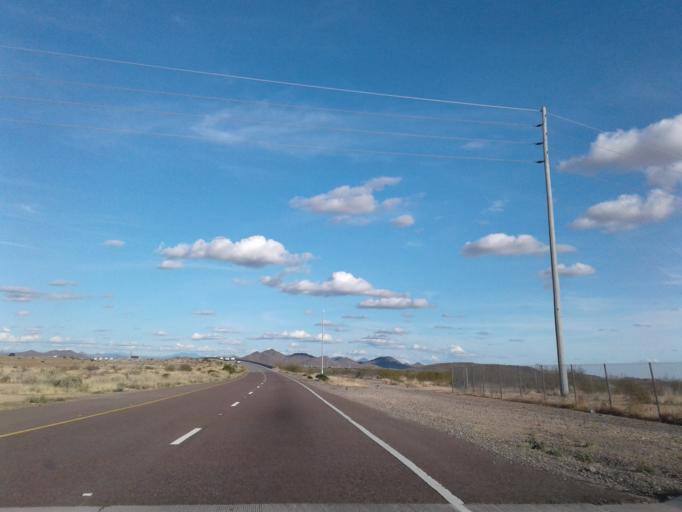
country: US
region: Arizona
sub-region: Maricopa County
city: Anthem
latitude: 33.7685
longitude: -112.1708
